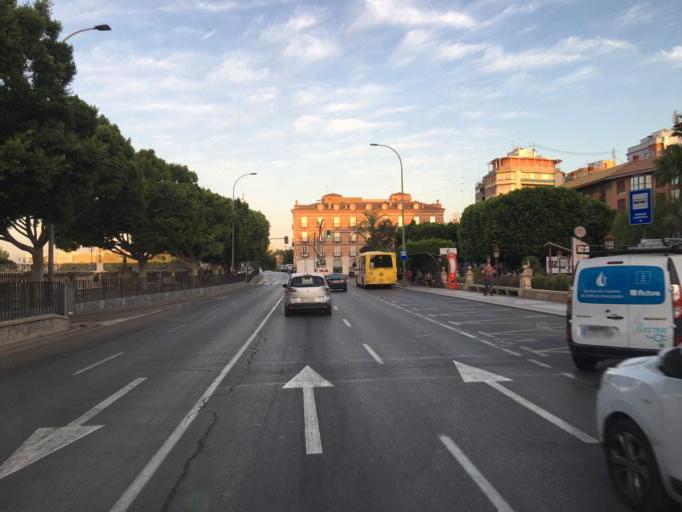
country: ES
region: Murcia
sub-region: Murcia
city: Murcia
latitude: 37.9830
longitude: -1.1303
